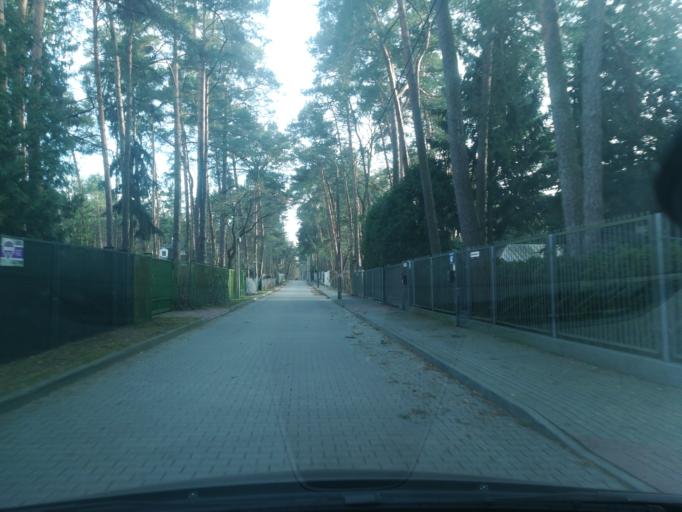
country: PL
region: Masovian Voivodeship
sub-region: Powiat piaseczynski
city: Konstancin-Jeziorna
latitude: 52.0820
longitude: 21.1065
